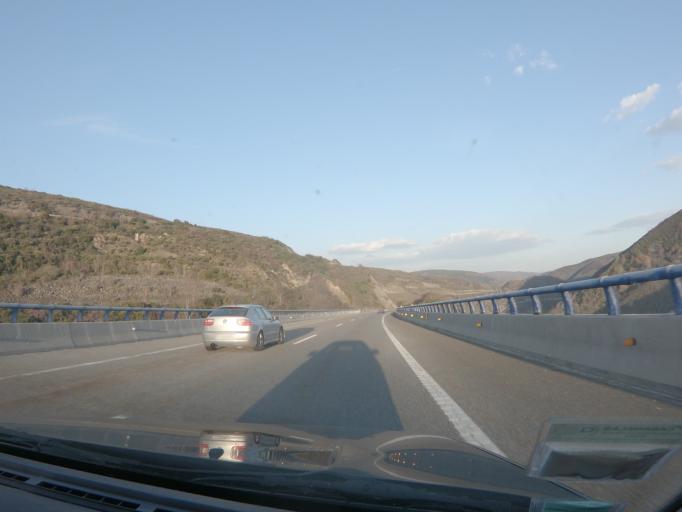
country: ES
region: Castille and Leon
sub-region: Provincia de Leon
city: Vega de Valcarce
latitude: 42.6744
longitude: -6.9797
